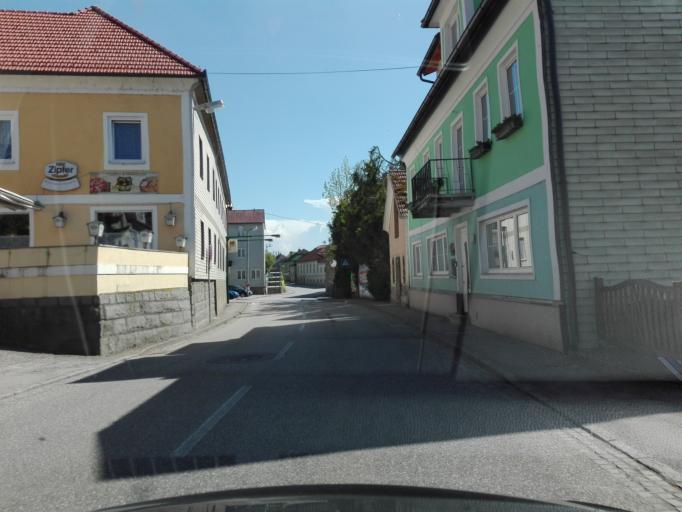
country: AT
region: Upper Austria
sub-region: Politischer Bezirk Grieskirchen
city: Bad Schallerbach
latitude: 48.3163
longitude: 13.9036
